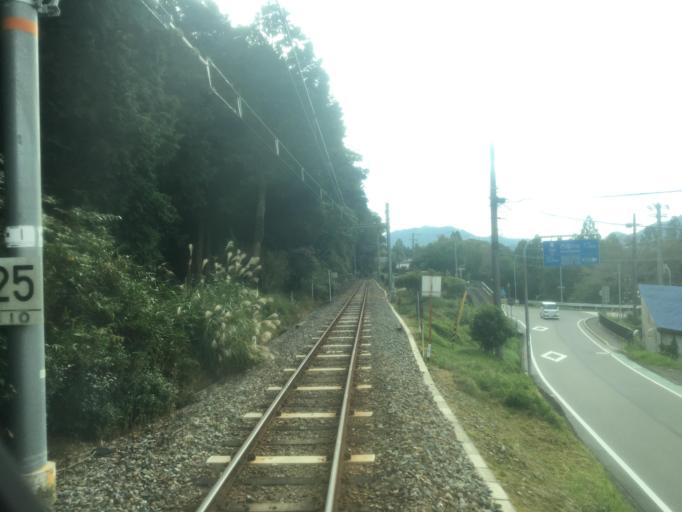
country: JP
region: Hyogo
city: Nishiwaki
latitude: 35.0628
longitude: 135.0090
